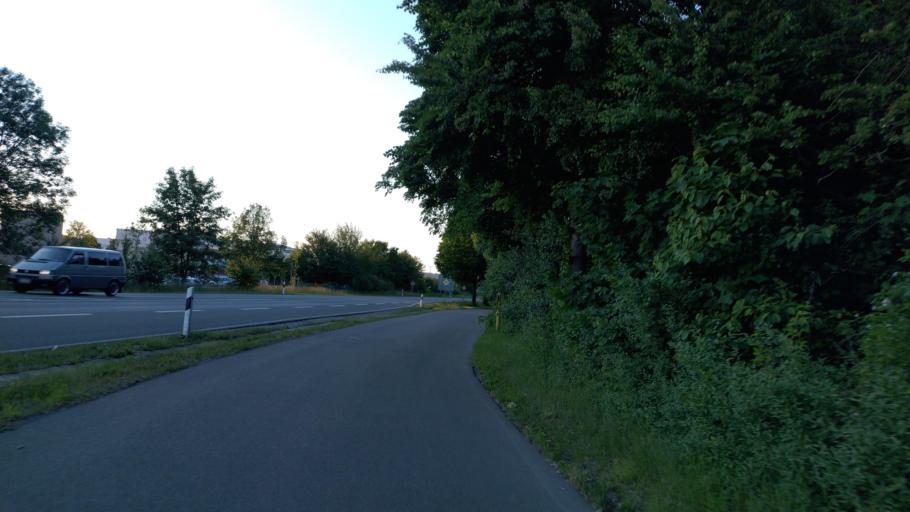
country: DE
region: Bavaria
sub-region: Upper Franconia
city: Bindlach
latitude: 49.9650
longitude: 11.6093
